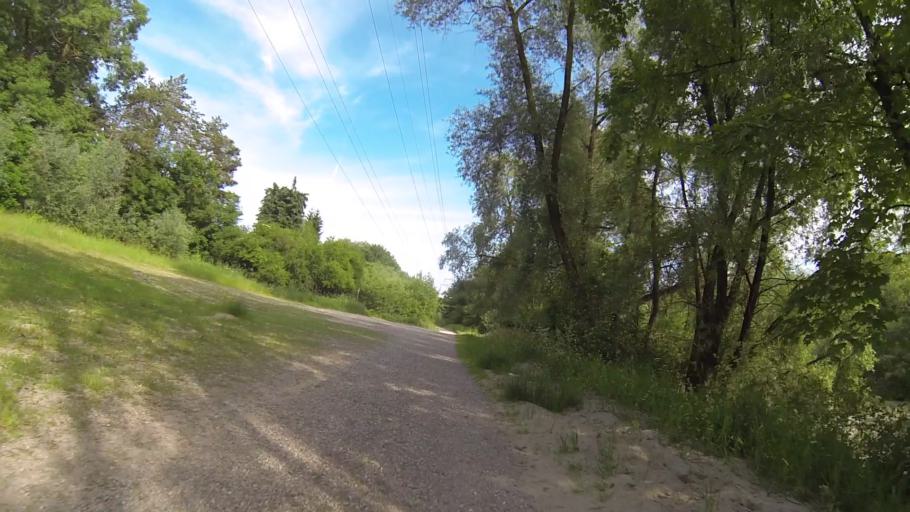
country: DE
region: Bavaria
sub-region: Swabia
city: Senden
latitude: 48.3247
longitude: 10.0243
